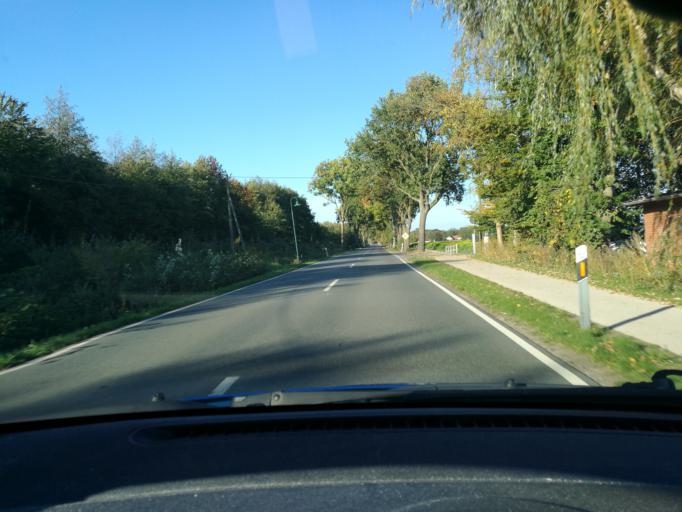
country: DE
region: Lower Saxony
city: Ludersburg
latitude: 53.3101
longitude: 10.5721
